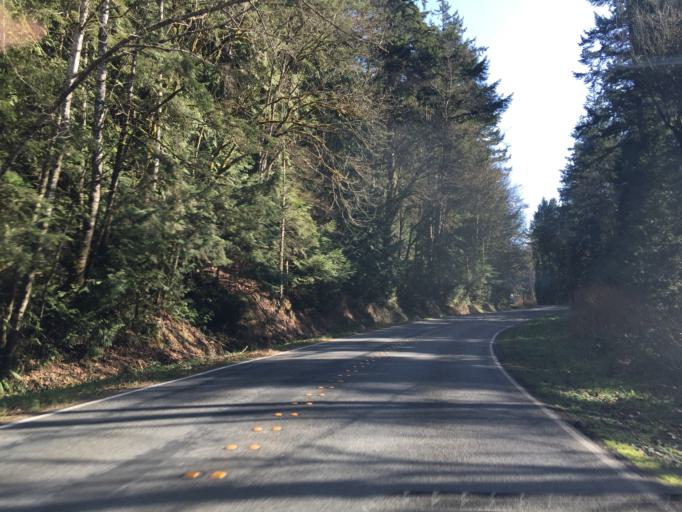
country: US
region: Washington
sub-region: Whatcom County
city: Bellingham
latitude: 48.7027
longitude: -122.4832
